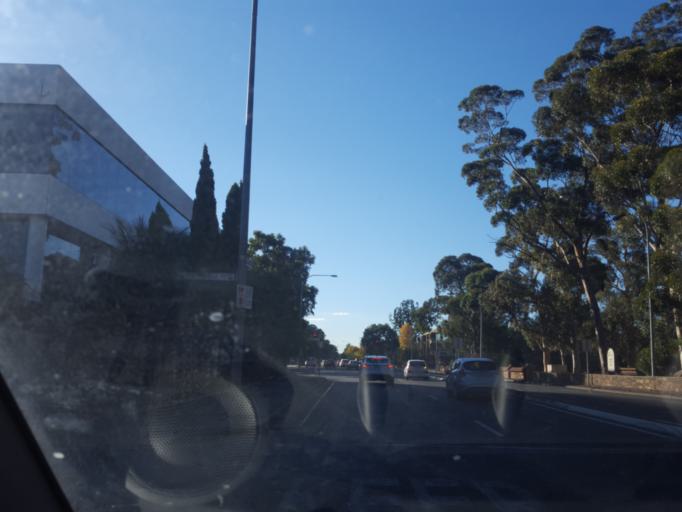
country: AU
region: South Australia
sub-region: Unley
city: Fullarton
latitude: -34.9417
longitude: 138.6246
